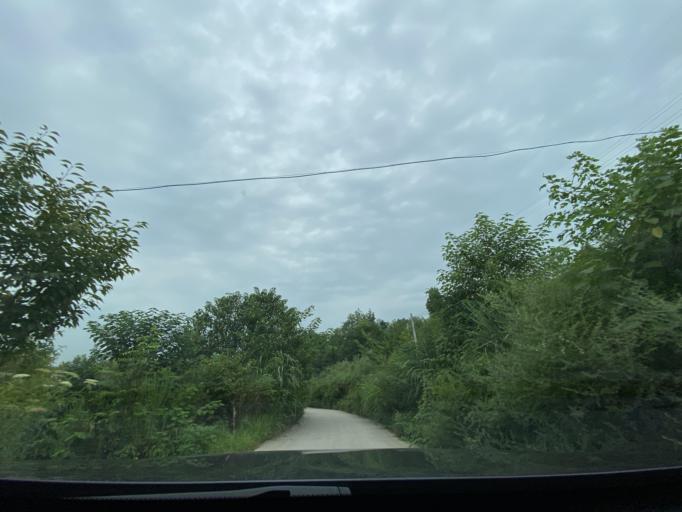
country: CN
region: Sichuan
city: Jiancheng
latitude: 30.3876
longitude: 104.4967
